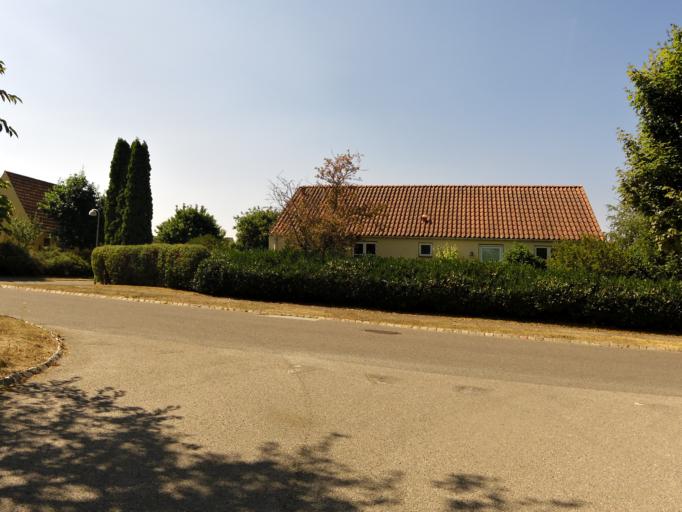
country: DK
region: Capital Region
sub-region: Fredensborg Kommune
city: Niva
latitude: 55.9452
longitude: 12.4921
